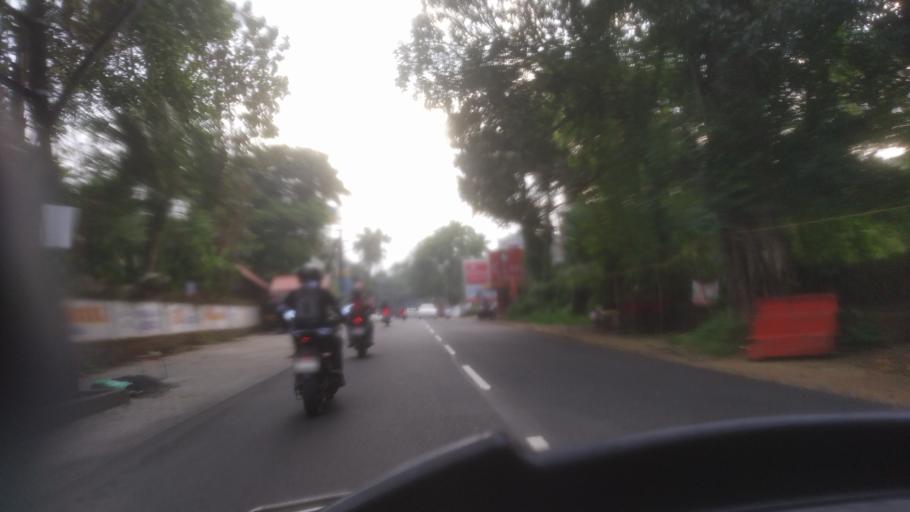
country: IN
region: Kerala
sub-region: Ernakulam
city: Kotamangalam
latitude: 10.0585
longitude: 76.6458
